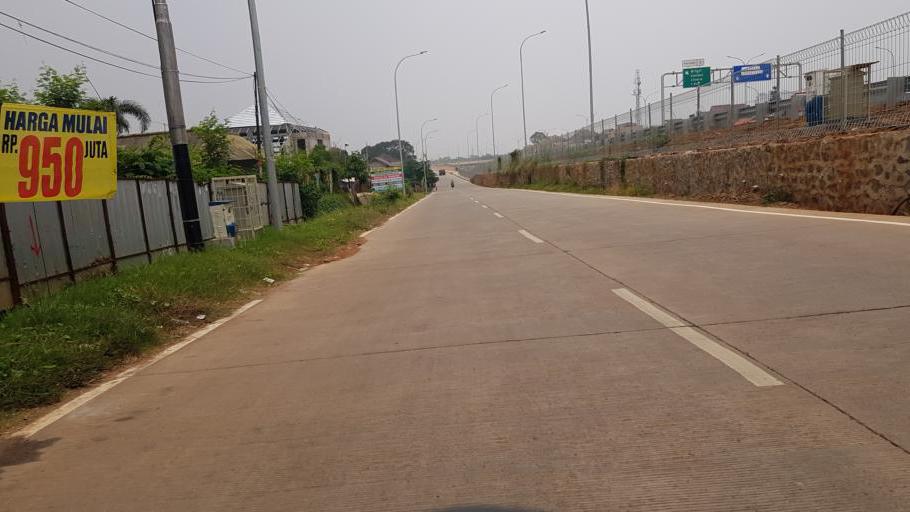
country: ID
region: West Java
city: Pamulang
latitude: -6.3281
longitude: 106.8013
